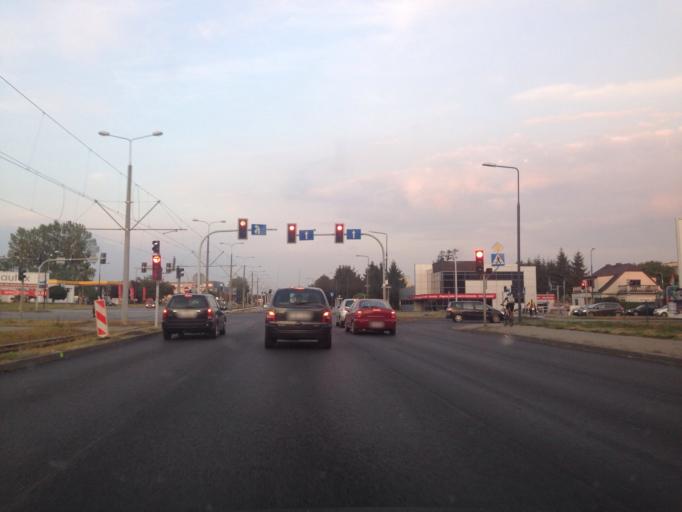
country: PL
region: Kujawsko-Pomorskie
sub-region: Bydgoszcz
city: Bydgoszcz
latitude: 53.1206
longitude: 18.0558
